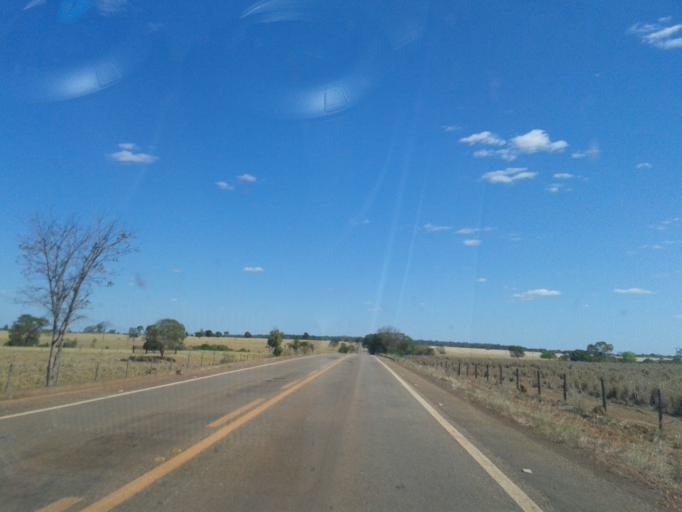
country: BR
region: Goias
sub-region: Sao Miguel Do Araguaia
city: Sao Miguel do Araguaia
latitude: -13.4441
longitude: -50.2913
